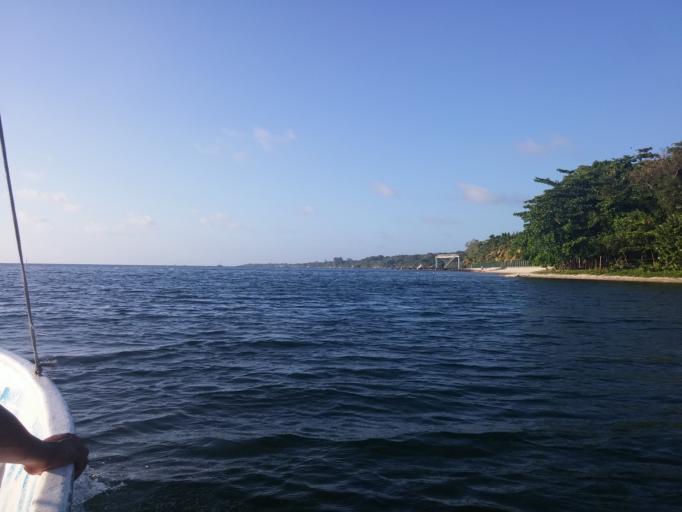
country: HN
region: Bay Islands
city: Sandy Bay
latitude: 16.2809
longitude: -86.6002
